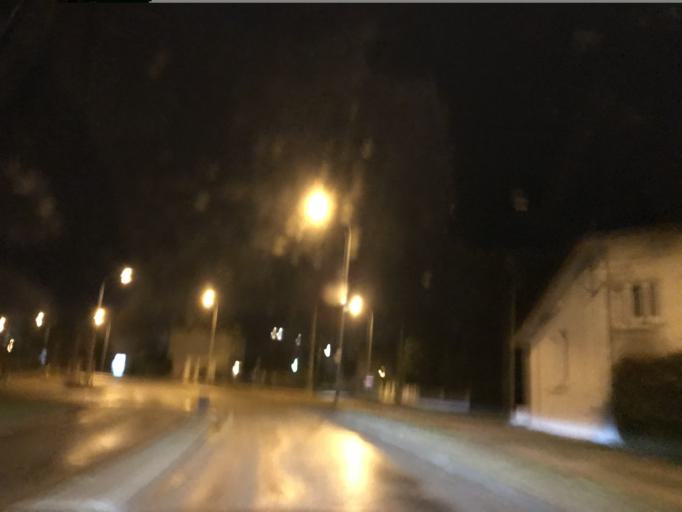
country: FR
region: Auvergne
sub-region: Departement de l'Allier
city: Vichy
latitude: 46.1127
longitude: 3.4200
